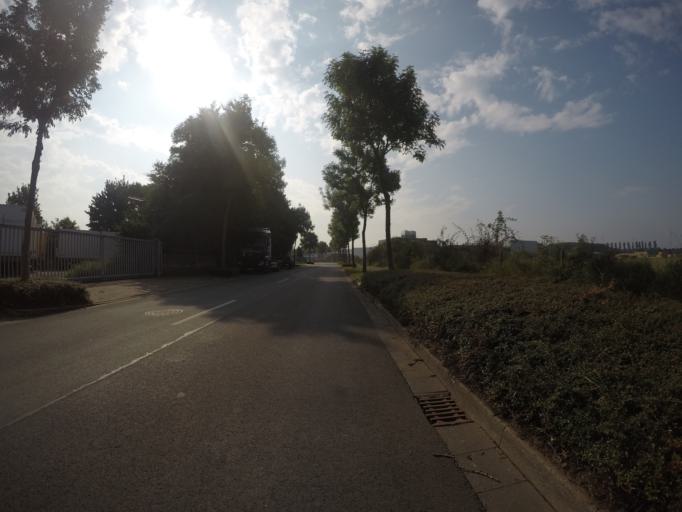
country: DE
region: North Rhine-Westphalia
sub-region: Regierungsbezirk Munster
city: Isselburg
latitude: 51.8144
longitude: 6.5388
